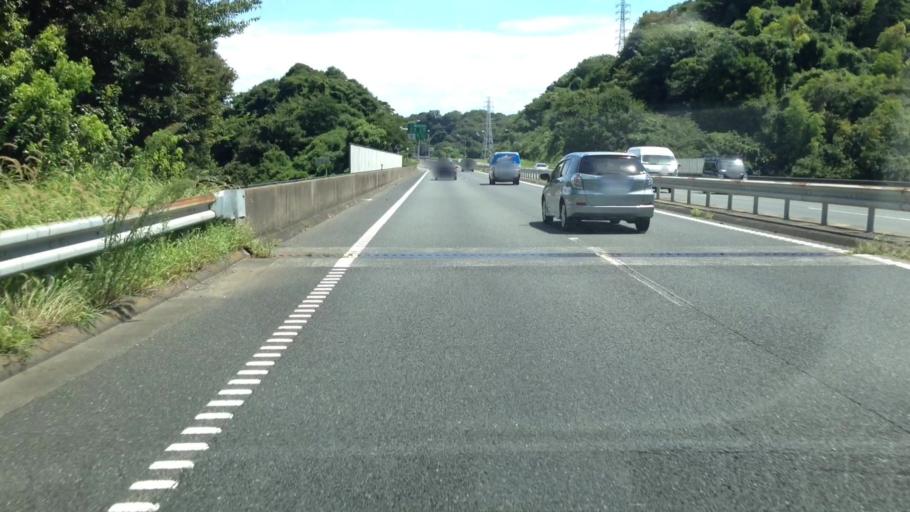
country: JP
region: Kanagawa
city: Yokosuka
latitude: 35.2434
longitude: 139.6546
